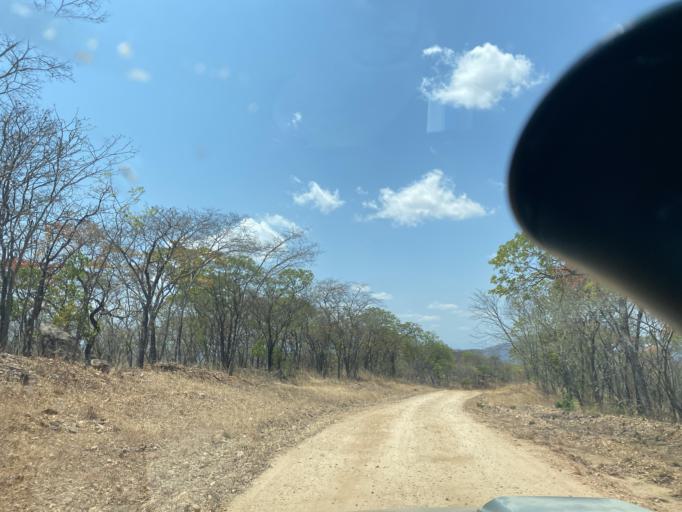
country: ZM
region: Lusaka
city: Luangwa
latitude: -15.0135
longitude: 29.7335
